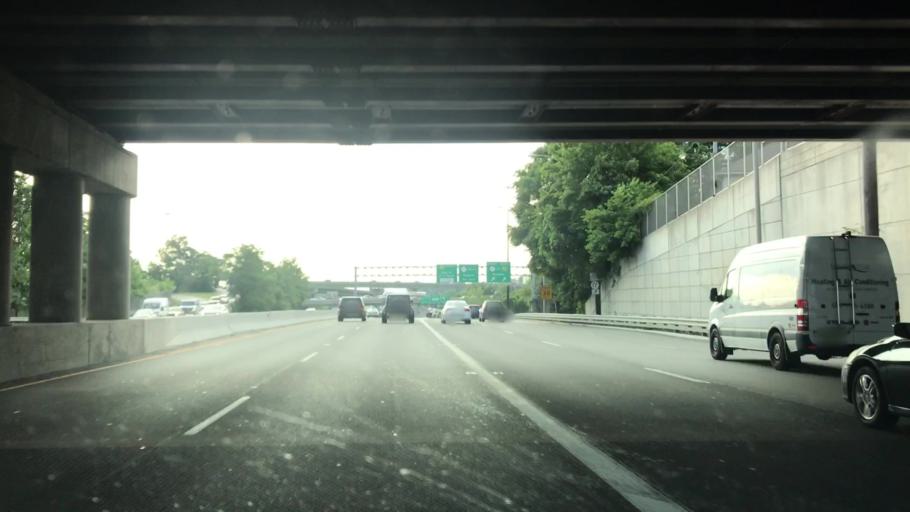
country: US
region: New Jersey
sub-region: Bergen County
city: Rochelle Park
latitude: 40.9205
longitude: -74.0690
